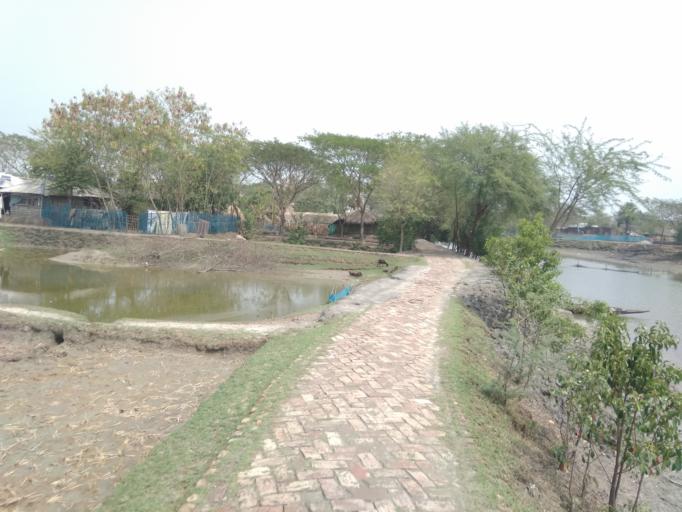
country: IN
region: West Bengal
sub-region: North 24 Parganas
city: Taki
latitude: 22.2578
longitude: 89.2579
